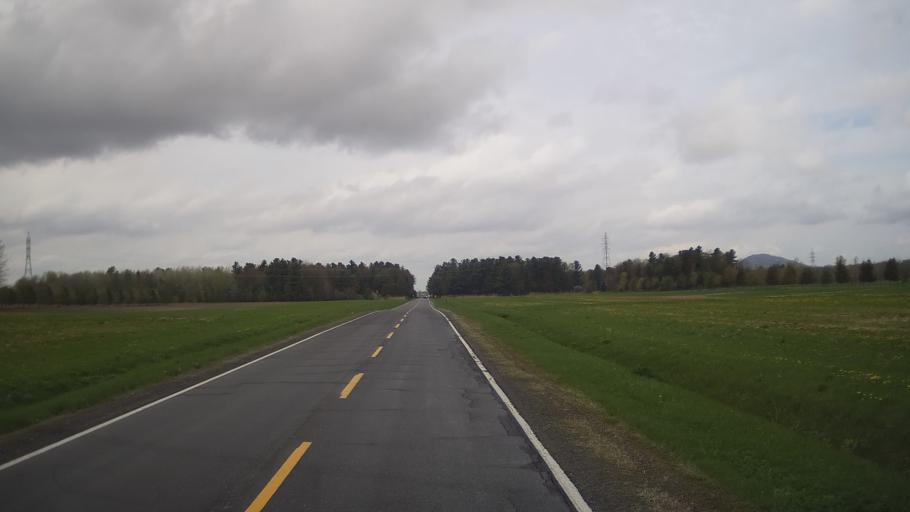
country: CA
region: Quebec
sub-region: Monteregie
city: Marieville
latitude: 45.3103
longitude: -73.1216
